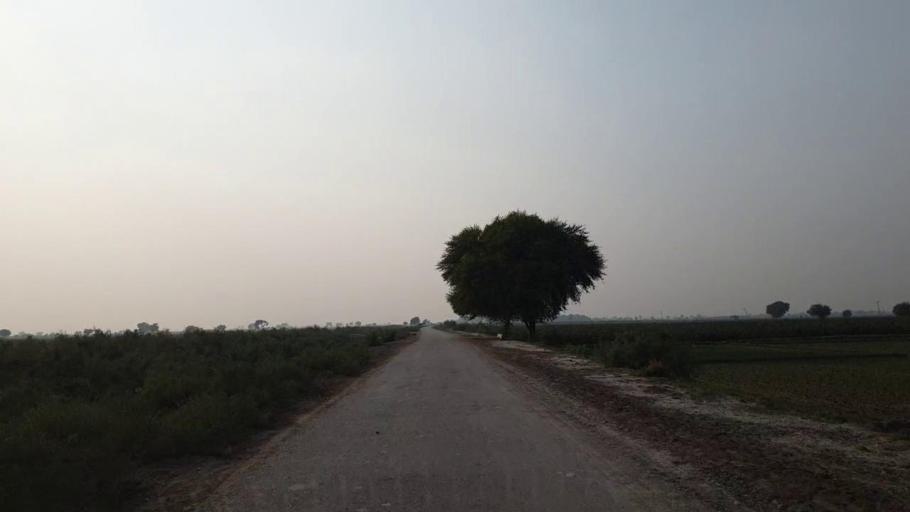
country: PK
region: Sindh
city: Bhan
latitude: 26.4884
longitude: 67.7161
